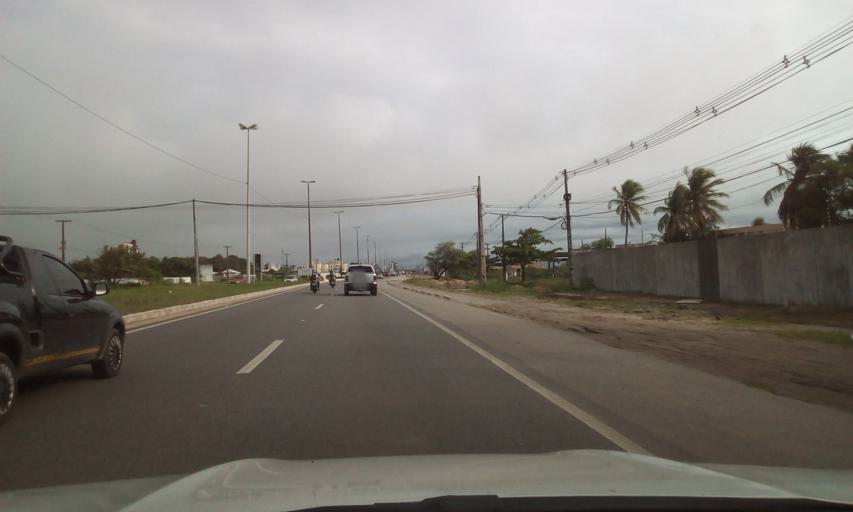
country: BR
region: Paraiba
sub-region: Cabedelo
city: Cabedelo
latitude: -7.0217
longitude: -34.8366
